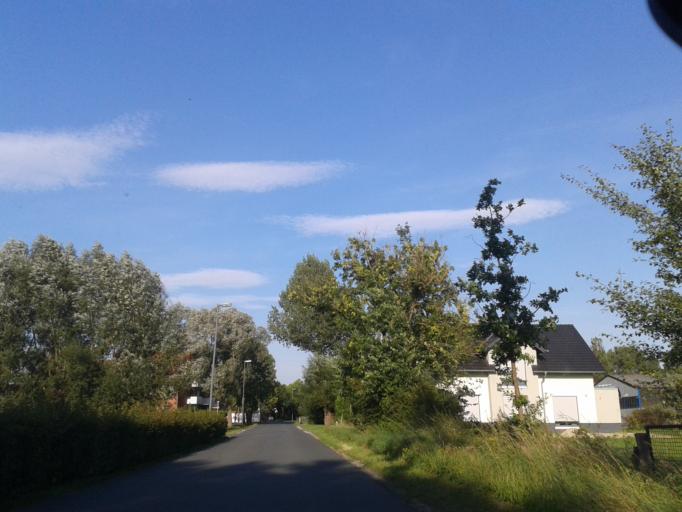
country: DE
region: North Rhine-Westphalia
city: Bad Lippspringe
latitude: 51.7741
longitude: 8.8156
